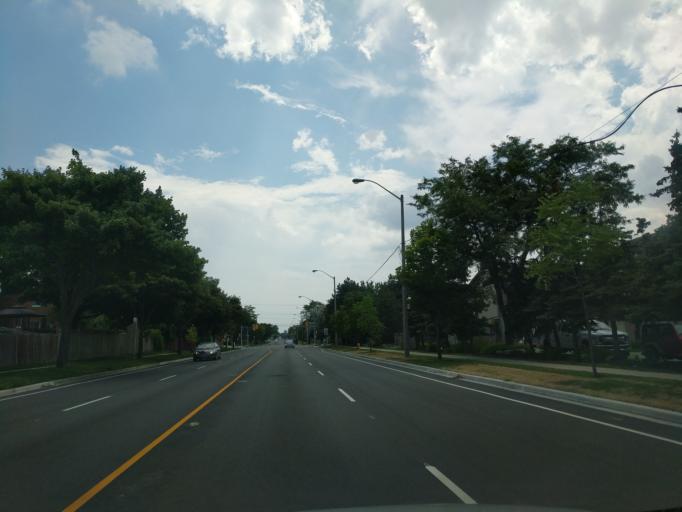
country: CA
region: Ontario
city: Scarborough
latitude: 43.8120
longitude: -79.3127
